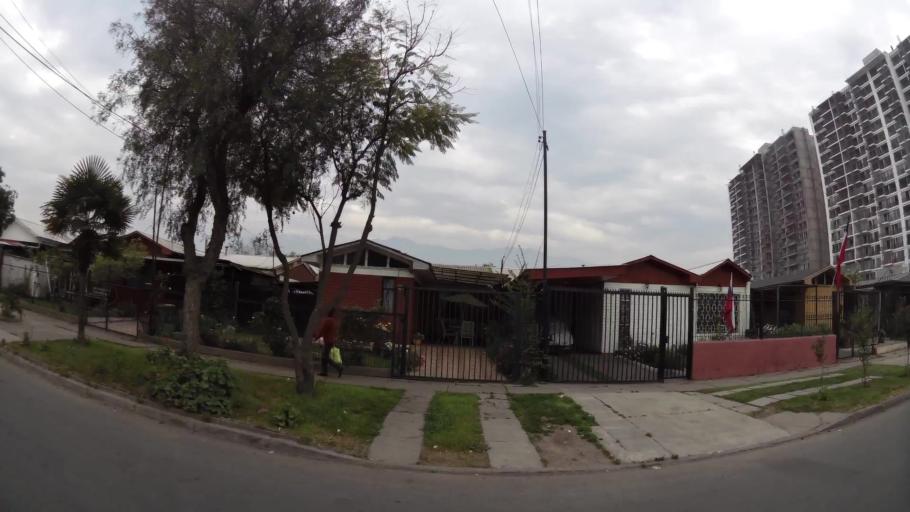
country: CL
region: Santiago Metropolitan
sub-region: Provincia de Santiago
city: Villa Presidente Frei, Nunoa, Santiago, Chile
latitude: -33.5131
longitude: -70.5942
